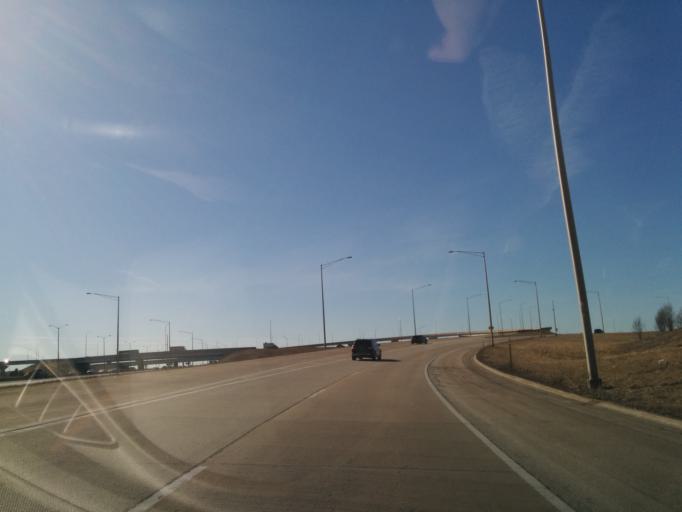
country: US
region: Illinois
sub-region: Cook County
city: Lemont
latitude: 41.7079
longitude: -88.0248
